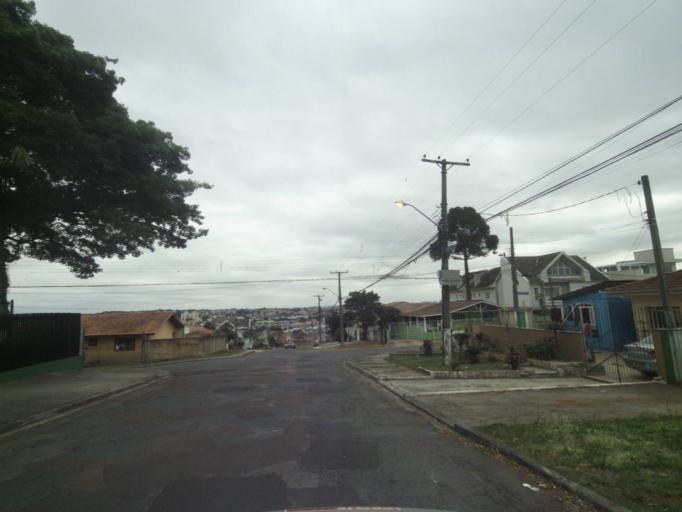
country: BR
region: Parana
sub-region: Sao Jose Dos Pinhais
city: Sao Jose dos Pinhais
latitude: -25.4837
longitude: -49.2321
